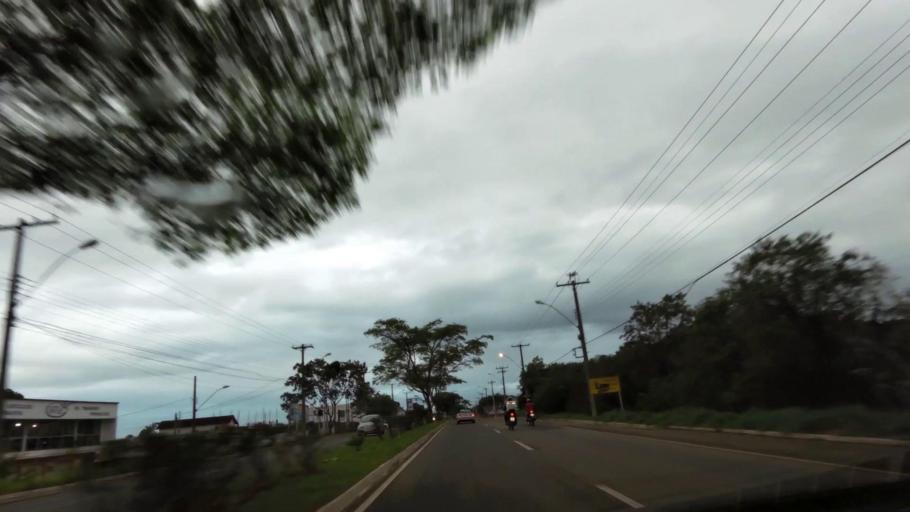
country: BR
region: Espirito Santo
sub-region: Guarapari
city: Guarapari
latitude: -20.6478
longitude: -40.5112
